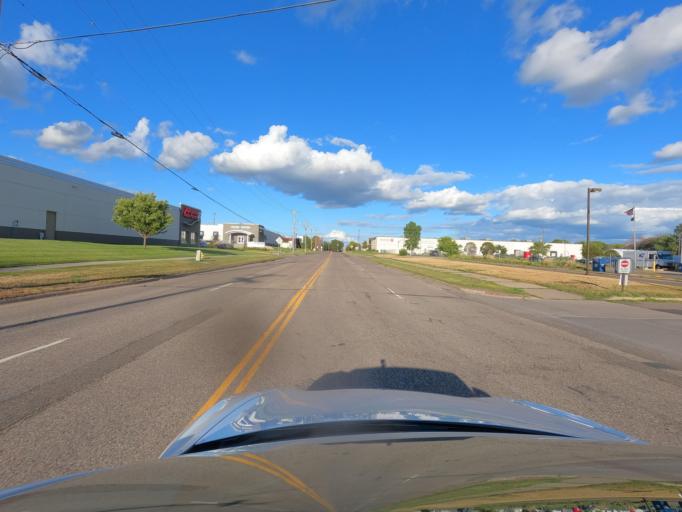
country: US
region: Minnesota
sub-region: Ramsey County
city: Lauderdale
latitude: 45.0149
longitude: -93.1853
